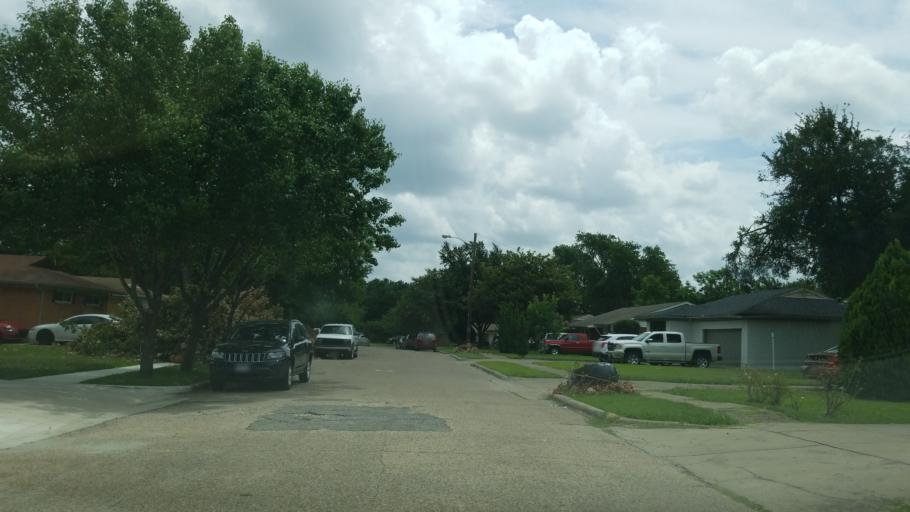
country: US
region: Texas
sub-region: Dallas County
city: Farmers Branch
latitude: 32.8887
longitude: -96.8794
